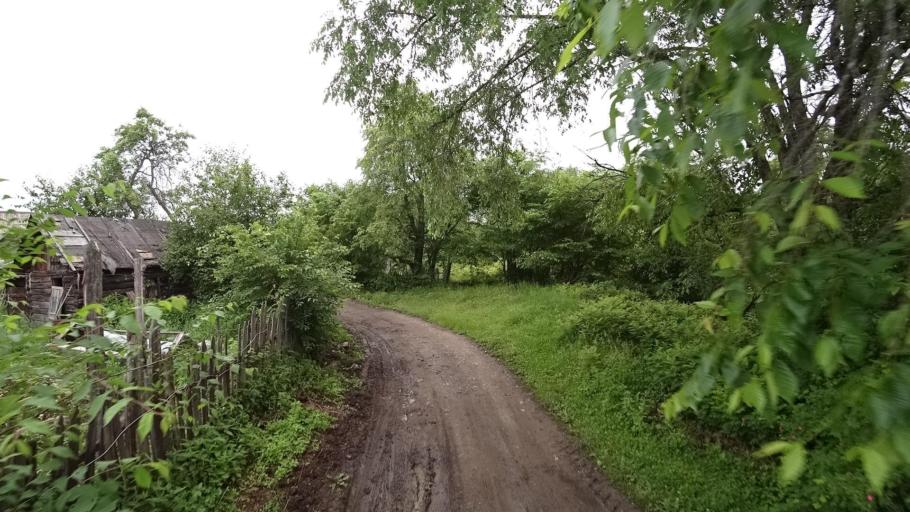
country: RU
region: Khabarovsk Krai
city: Amursk
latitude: 49.9063
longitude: 136.1330
